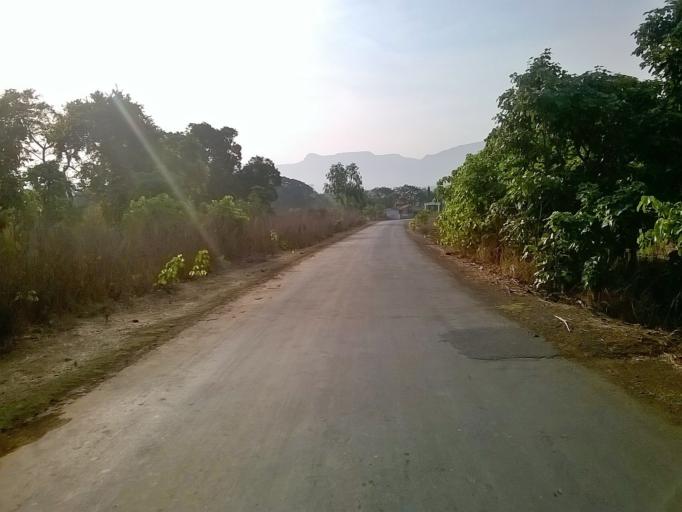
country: IN
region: Maharashtra
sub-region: Raigarh
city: Matheran
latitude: 19.0294
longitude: 73.2174
